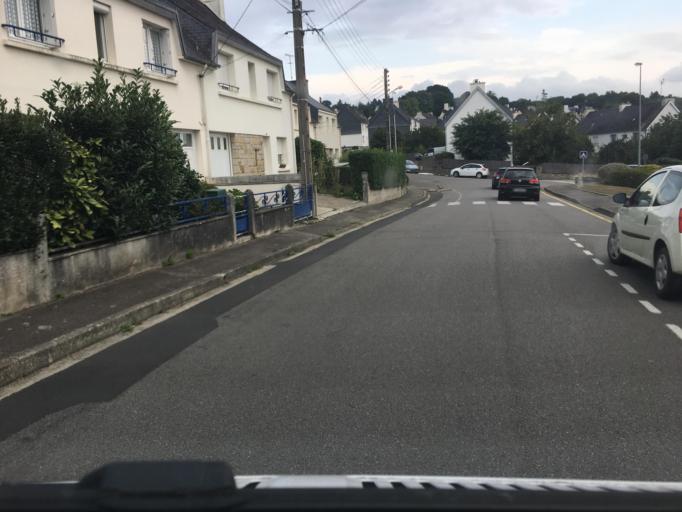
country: FR
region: Brittany
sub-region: Departement du Finistere
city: Chateaulin
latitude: 48.1995
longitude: -4.0903
